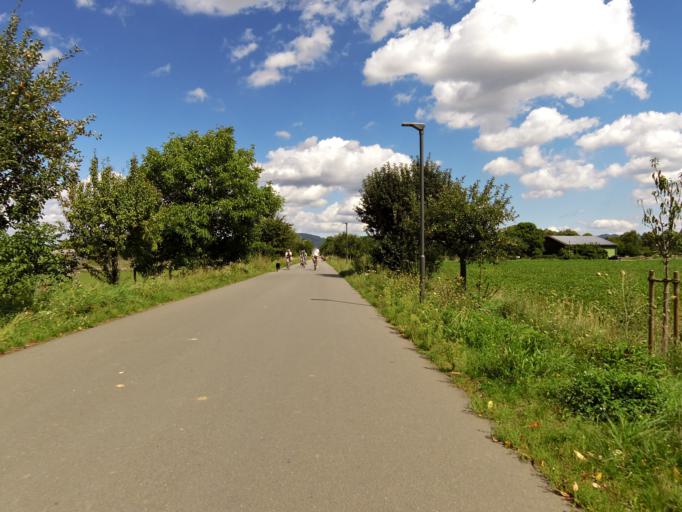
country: DE
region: Hesse
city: Lorsch
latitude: 49.6561
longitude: 8.5741
